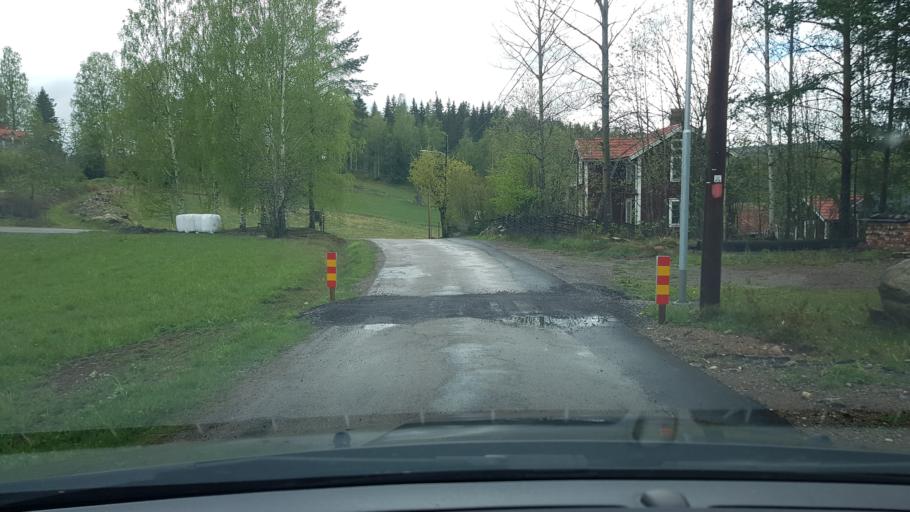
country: SE
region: Dalarna
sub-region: Faluns Kommun
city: Bjursas
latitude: 60.7339
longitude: 15.4538
